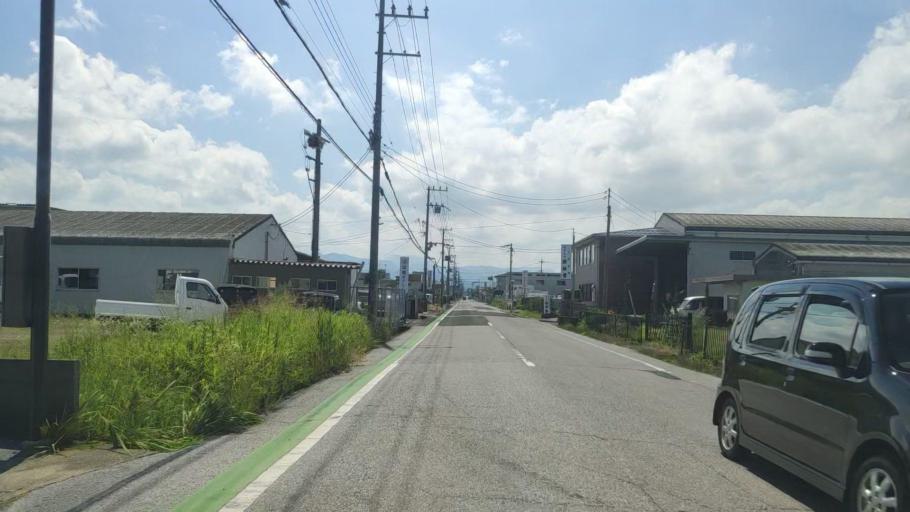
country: JP
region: Shiga Prefecture
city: Hikone
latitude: 35.2645
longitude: 136.2321
